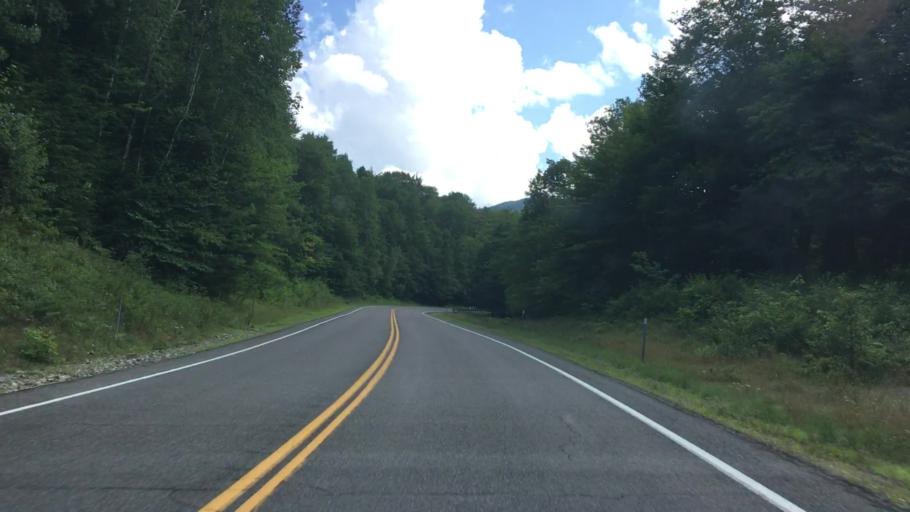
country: US
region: New Hampshire
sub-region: Grafton County
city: Woodstock
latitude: 44.0606
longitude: -71.7926
